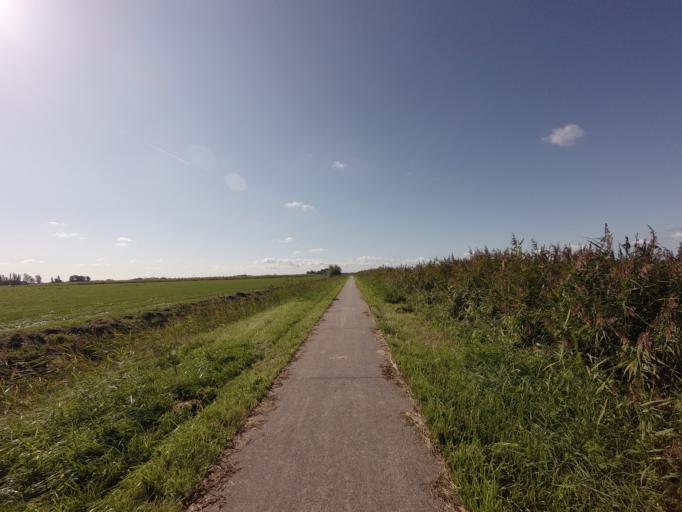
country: NL
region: Friesland
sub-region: Gemeente Boarnsterhim
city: Reduzum
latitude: 53.1351
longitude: 5.7588
